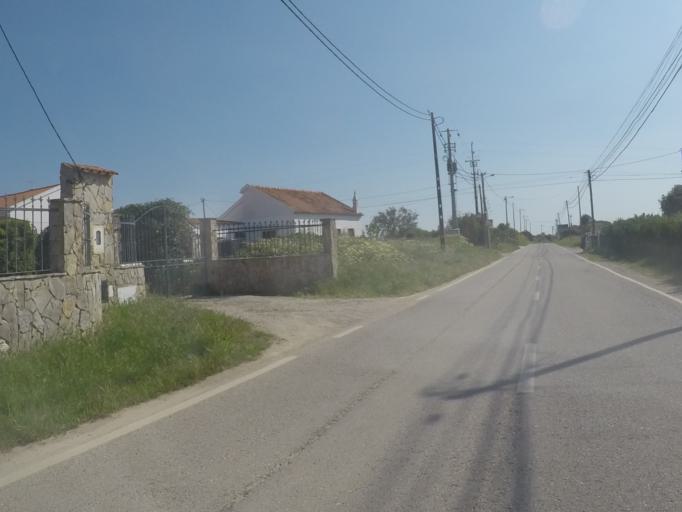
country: PT
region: Setubal
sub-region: Sesimbra
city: Sesimbra
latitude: 38.4375
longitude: -9.1776
